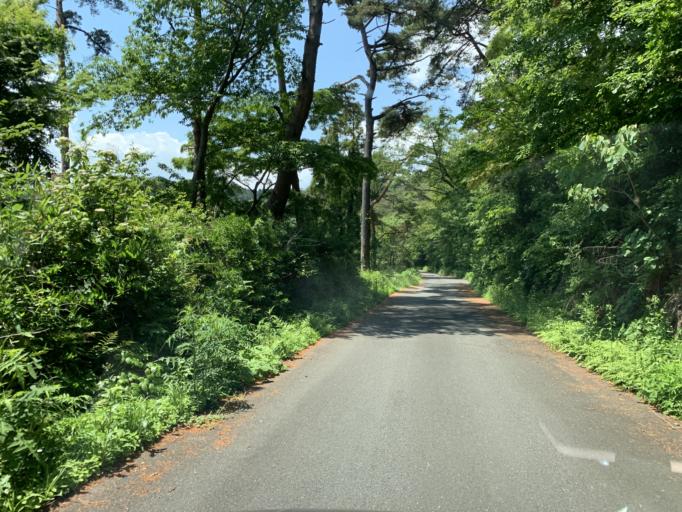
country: JP
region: Miyagi
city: Matsushima
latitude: 38.3522
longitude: 141.0620
